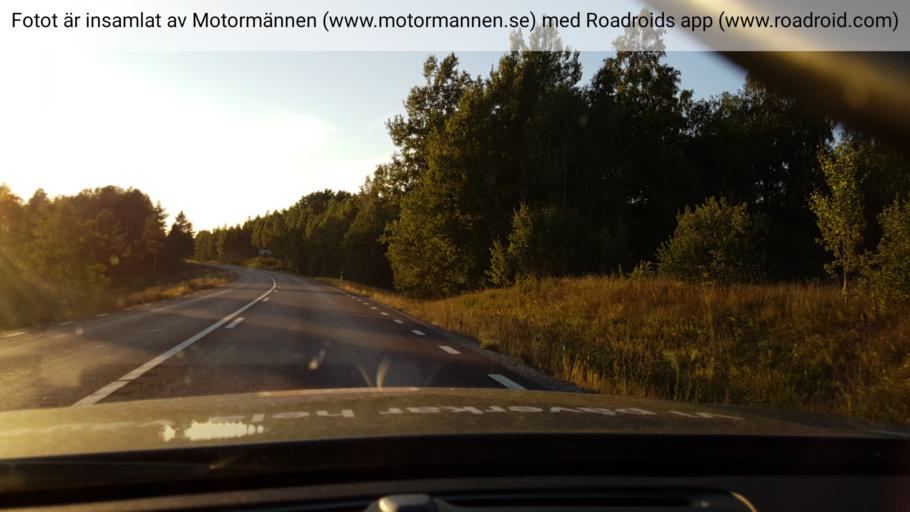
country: SE
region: OErebro
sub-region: Karlskoga Kommun
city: Karlskoga
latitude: 59.4291
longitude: 14.4243
